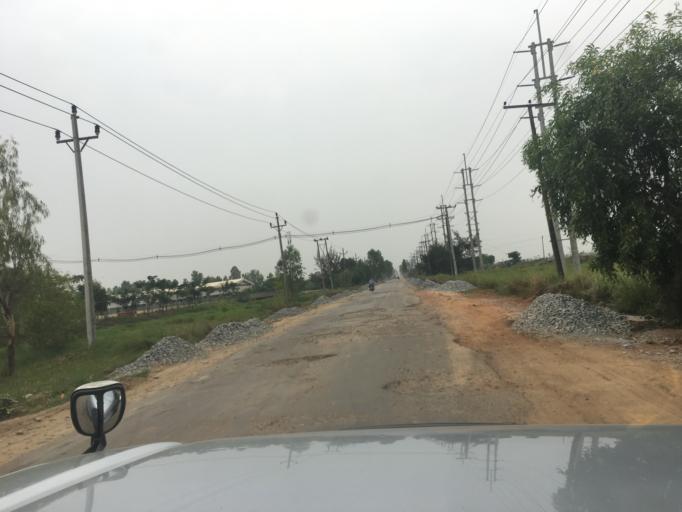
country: MM
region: Yangon
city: Yangon
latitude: 16.9550
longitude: 96.2689
